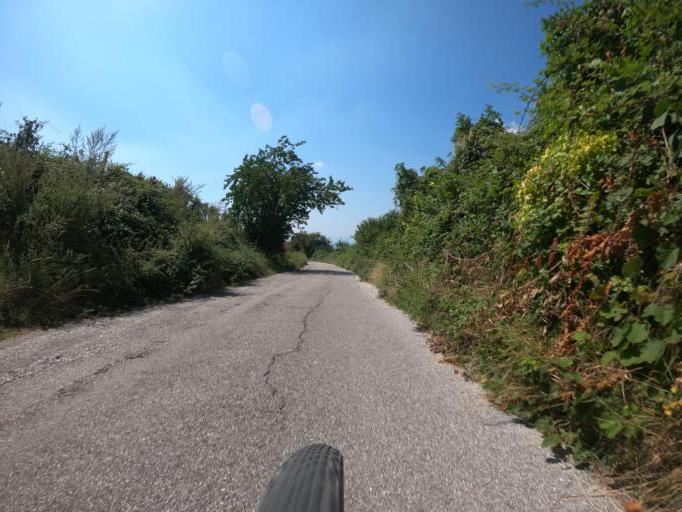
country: IT
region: Veneto
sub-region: Provincia di Verona
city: Ferrara di Monte Baldo
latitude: 45.6423
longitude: 10.8462
